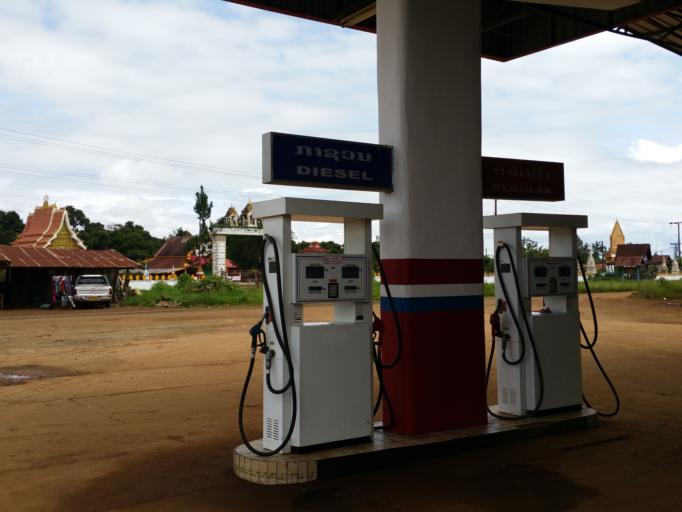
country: LA
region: Champasak
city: Pakxong
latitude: 15.2105
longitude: 106.3024
